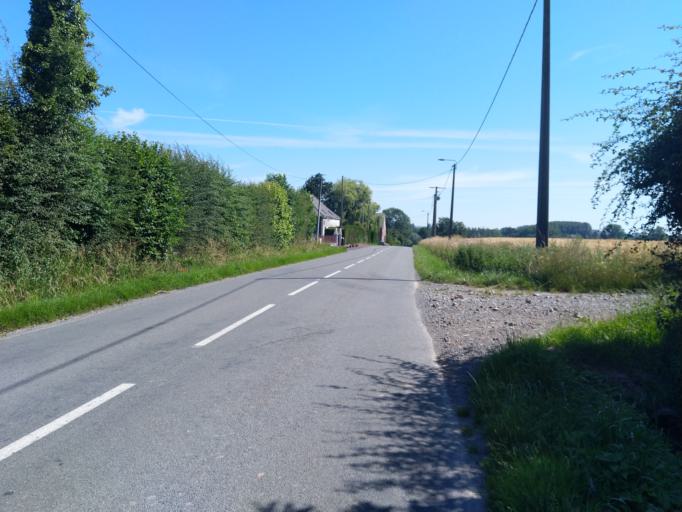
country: FR
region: Nord-Pas-de-Calais
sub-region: Departement du Nord
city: Bavay
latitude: 50.3205
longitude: 3.8206
